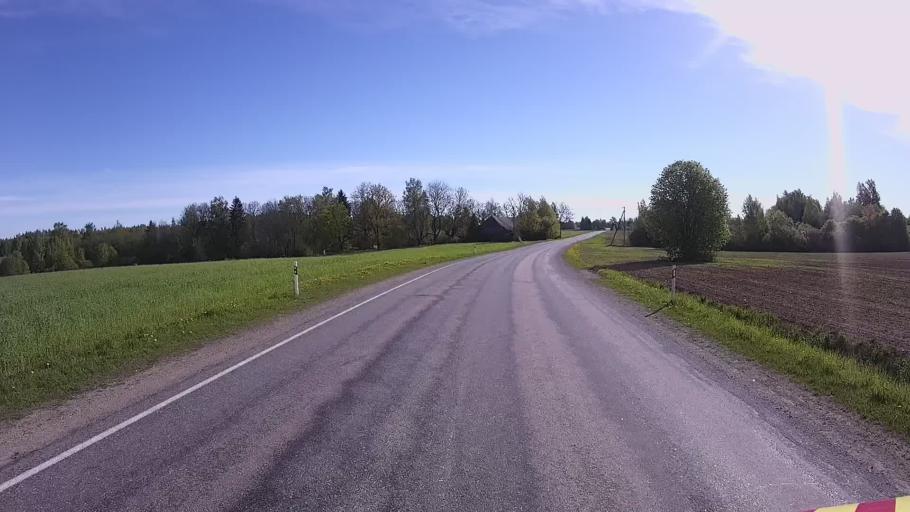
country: EE
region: Tartu
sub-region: Noo vald
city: Noo
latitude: 58.2120
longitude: 26.5923
